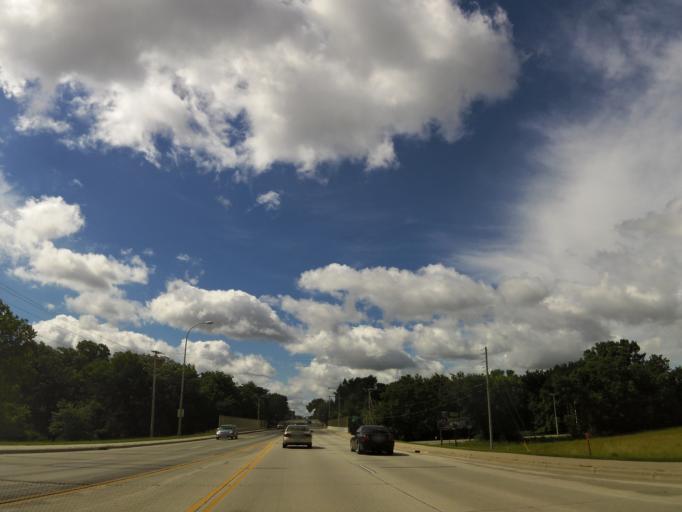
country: US
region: Minnesota
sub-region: Olmsted County
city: Stewartville
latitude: 43.8612
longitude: -92.4885
